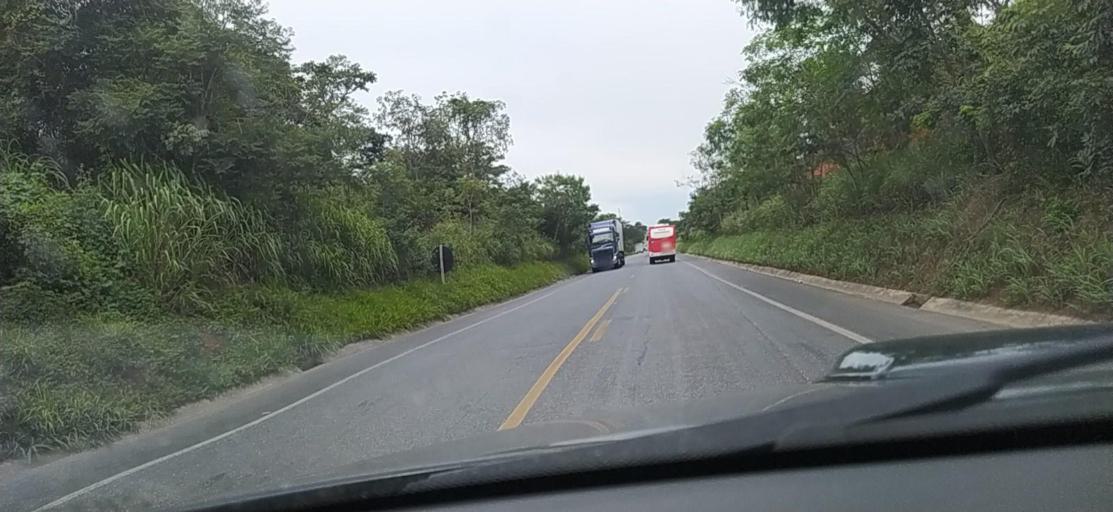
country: BR
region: Minas Gerais
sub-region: Montes Claros
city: Montes Claros
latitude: -16.6639
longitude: -43.7802
